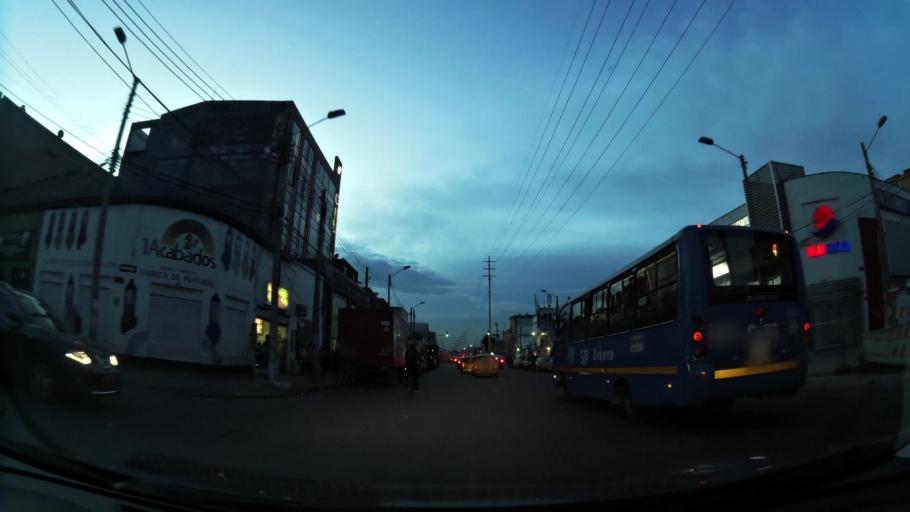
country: CO
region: Bogota D.C.
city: Barrio San Luis
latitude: 4.6586
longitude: -74.0690
